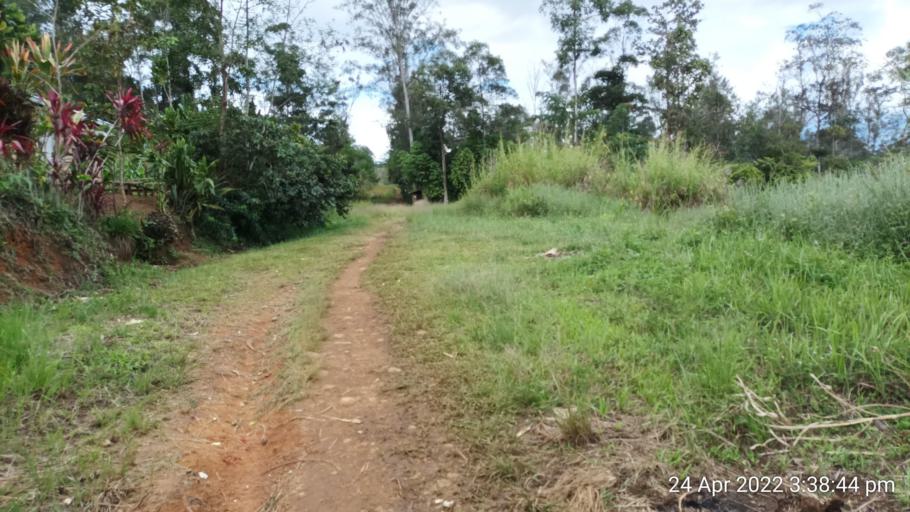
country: PG
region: Jiwaka
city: Minj
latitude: -5.8932
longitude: 144.8211
